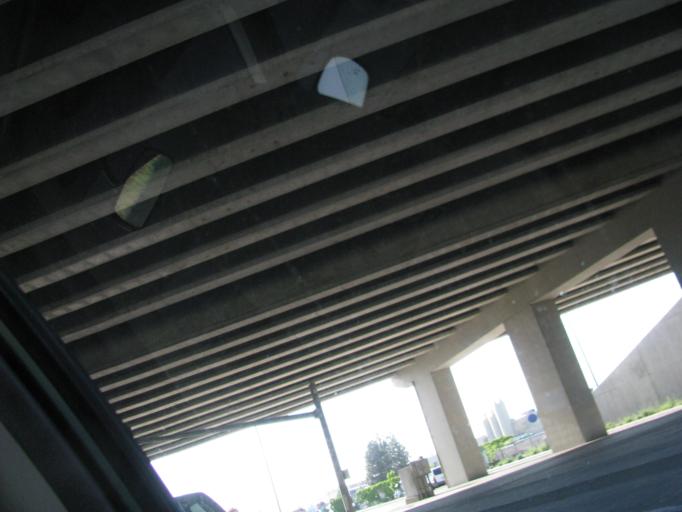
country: US
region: Washington
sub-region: Spokane County
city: Dishman
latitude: 47.6569
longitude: -117.3217
